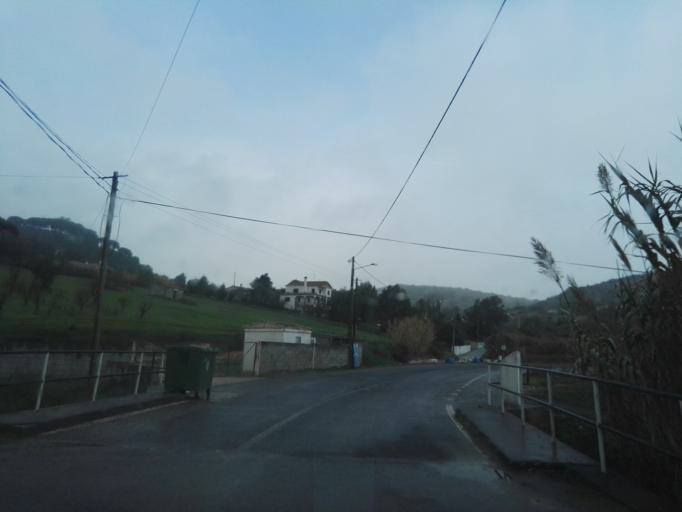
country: PT
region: Lisbon
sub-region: Vila Franca de Xira
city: Sobralinho
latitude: 38.9309
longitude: -9.0636
